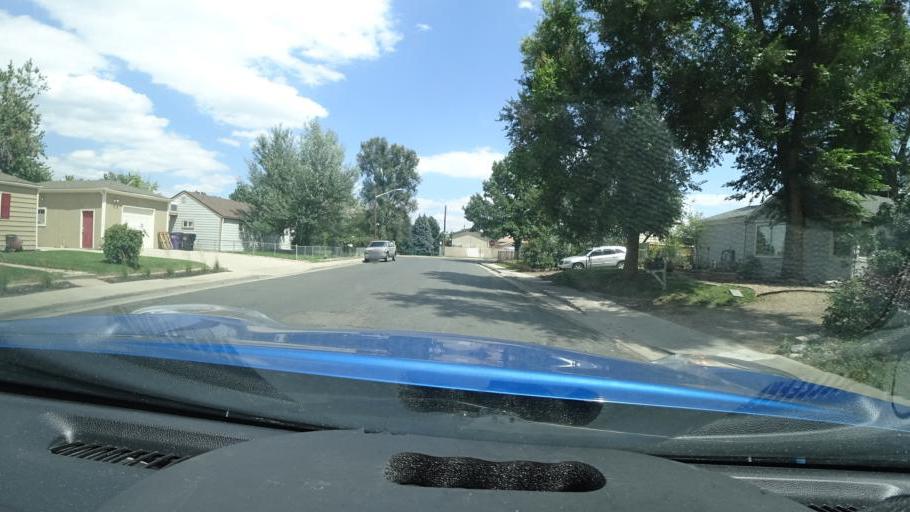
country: US
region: Colorado
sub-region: Arapahoe County
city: Sheridan
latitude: 39.6701
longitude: -105.0234
